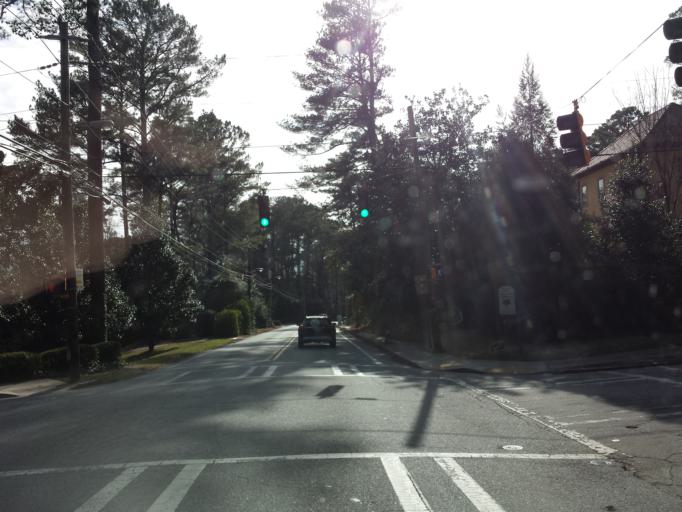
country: US
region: Georgia
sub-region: Cobb County
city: Vinings
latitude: 33.8275
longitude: -84.4393
